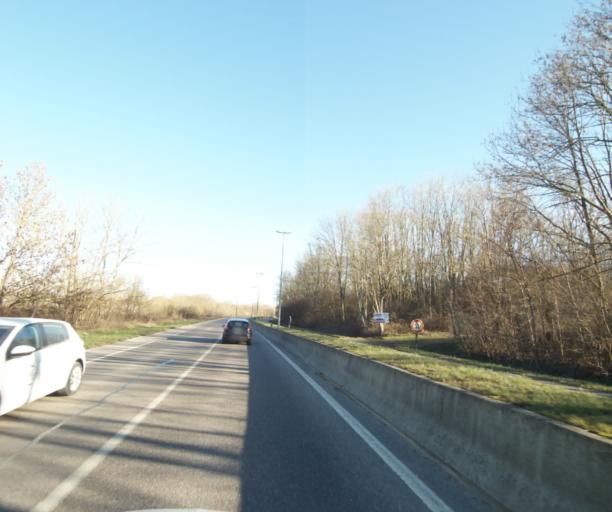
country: FR
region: Lorraine
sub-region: Departement de Meurthe-et-Moselle
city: Laneuveville-devant-Nancy
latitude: 48.6467
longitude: 6.2443
